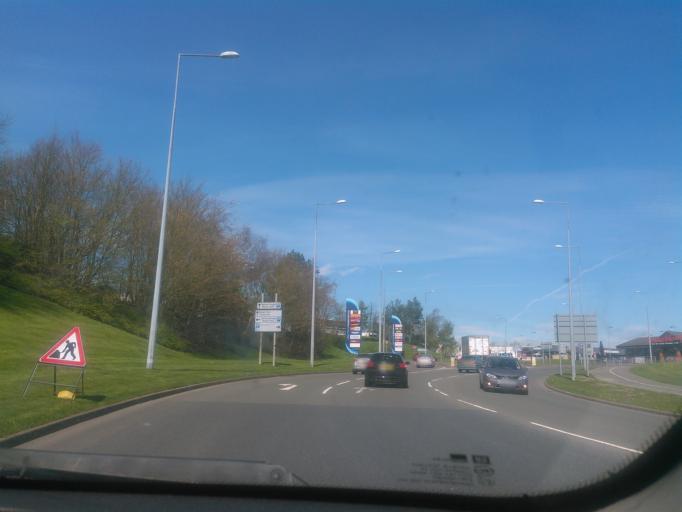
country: GB
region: England
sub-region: Telford and Wrekin
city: Telford
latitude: 52.6795
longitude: -2.4524
